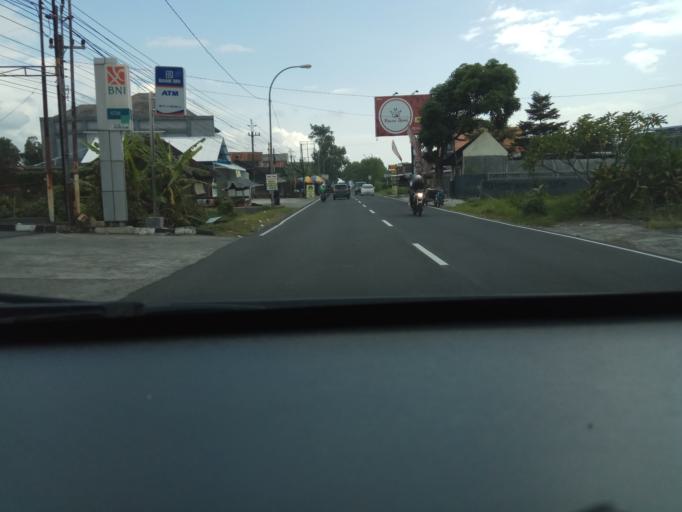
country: ID
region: Daerah Istimewa Yogyakarta
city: Melati
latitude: -7.7107
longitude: 110.4090
